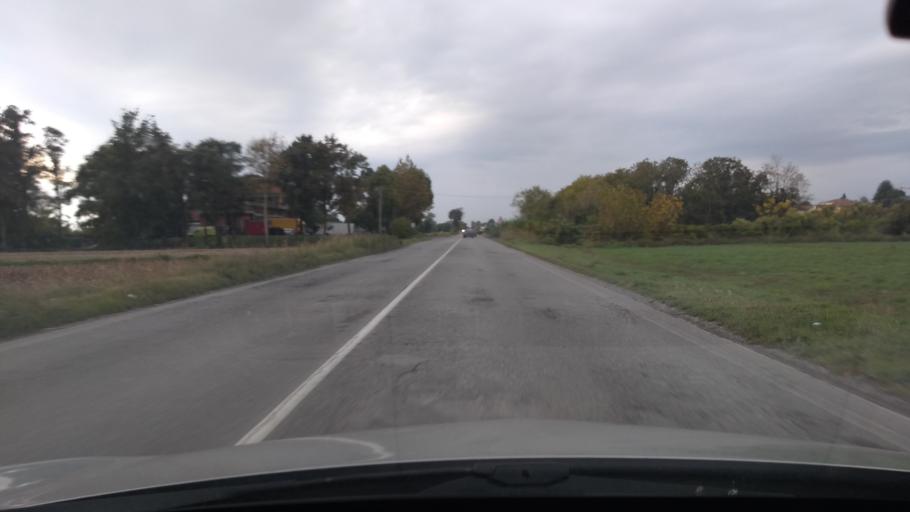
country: IT
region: Lombardy
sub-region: Provincia di Bergamo
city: Urgnano
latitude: 45.5911
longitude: 9.6941
